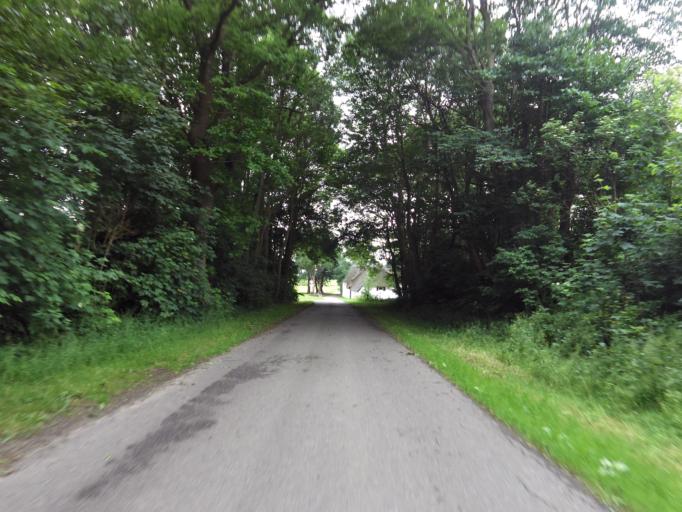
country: DK
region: South Denmark
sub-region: Tonder Kommune
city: Toftlund
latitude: 55.1027
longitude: 9.0863
